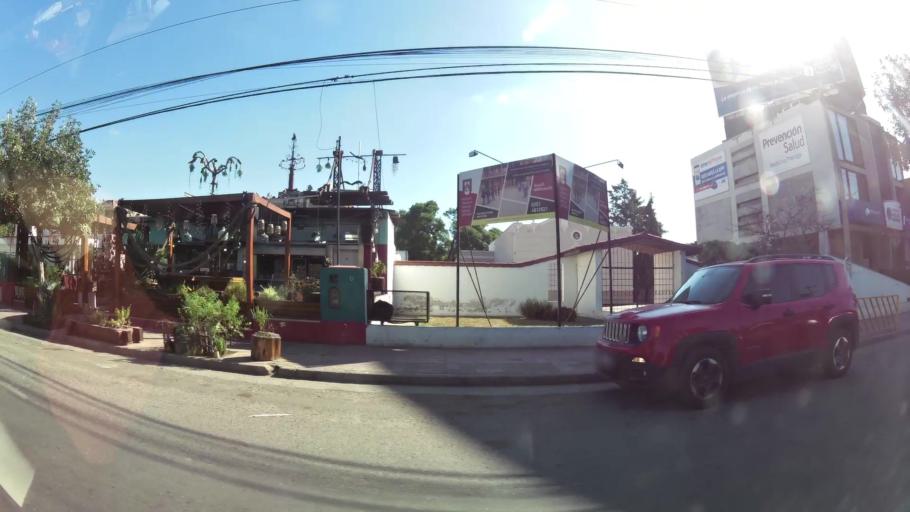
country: AR
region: Cordoba
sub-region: Departamento de Capital
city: Cordoba
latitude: -31.3598
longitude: -64.2389
